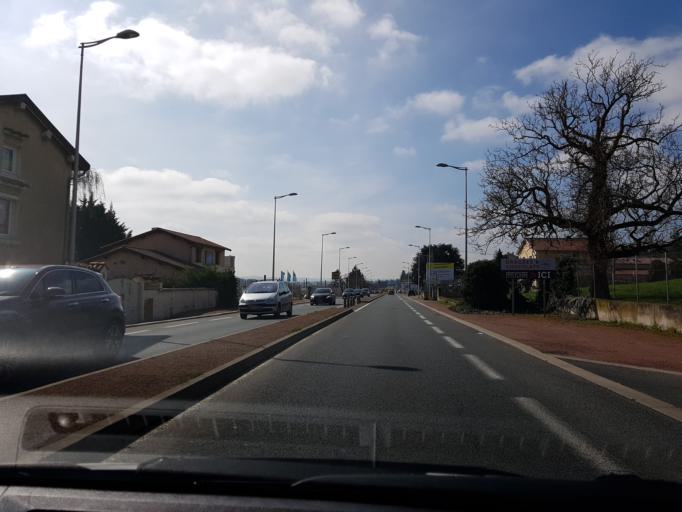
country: FR
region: Rhone-Alpes
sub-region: Departement du Rhone
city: Villefranche-sur-Saone
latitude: 45.9684
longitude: 4.7166
